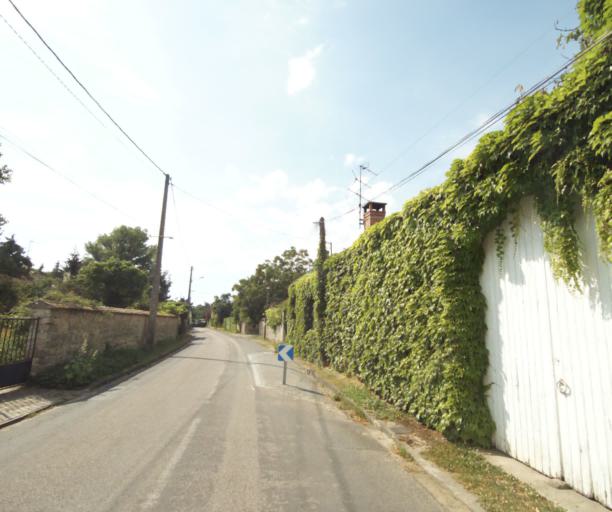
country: FR
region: Ile-de-France
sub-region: Departement de Seine-et-Marne
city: Acheres-la-Foret
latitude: 48.3532
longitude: 2.5722
